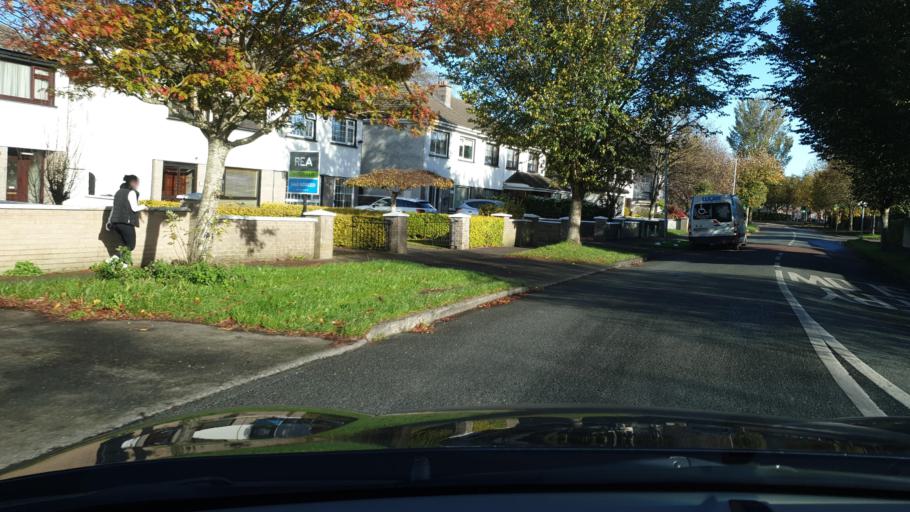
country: IE
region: Leinster
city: Lucan
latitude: 53.3502
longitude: -6.4400
